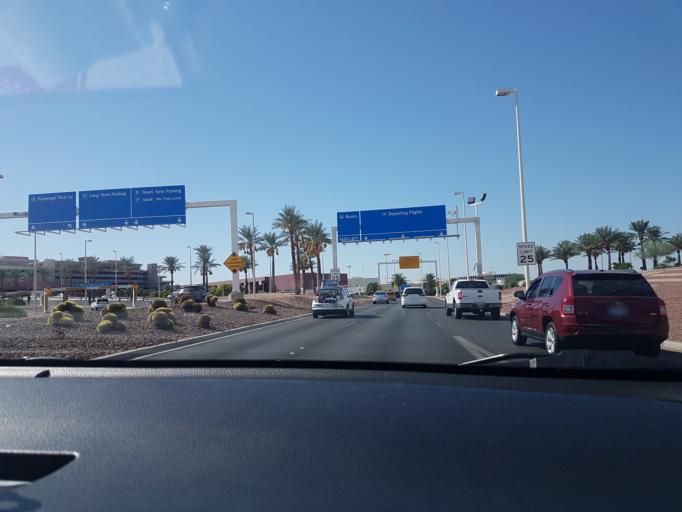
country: US
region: Nevada
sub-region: Clark County
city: Paradise
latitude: 36.0892
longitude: -115.1498
